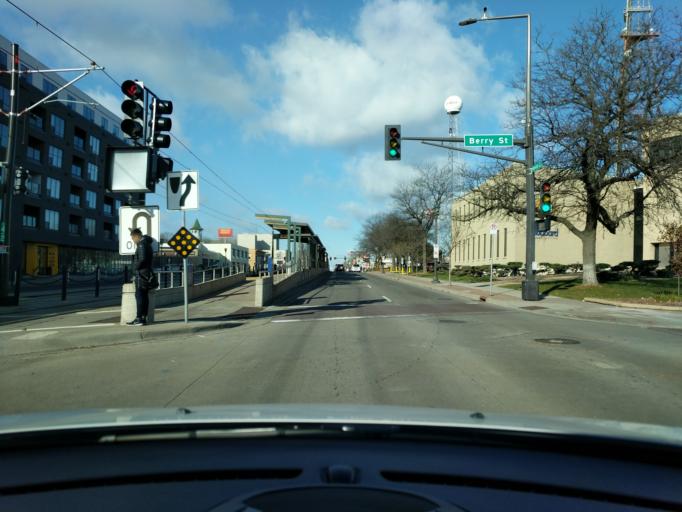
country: US
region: Minnesota
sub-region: Ramsey County
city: Lauderdale
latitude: 44.9676
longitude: -93.2065
